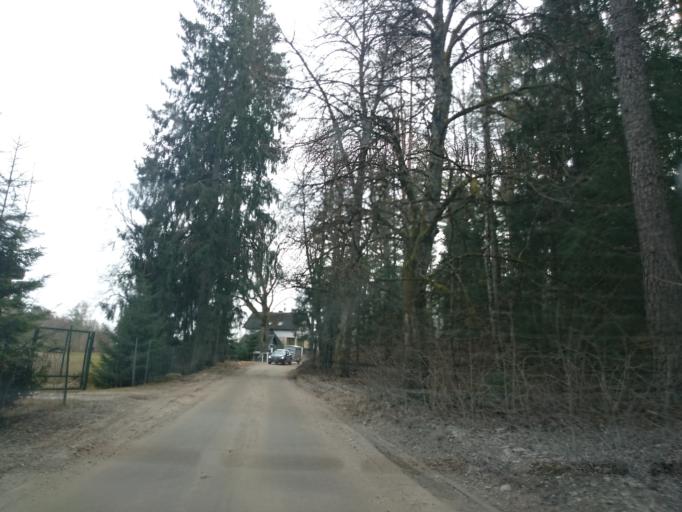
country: LV
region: Garkalne
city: Garkalne
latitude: 57.0219
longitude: 24.3870
